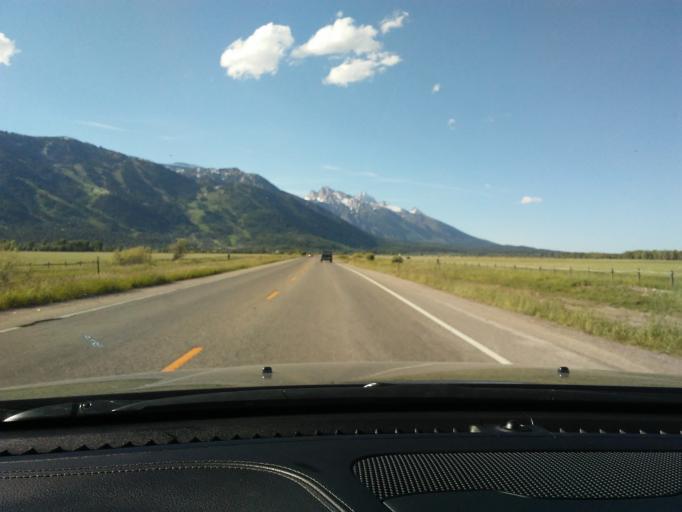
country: US
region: Wyoming
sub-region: Teton County
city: Moose Wilson Road
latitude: 43.5604
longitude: -110.8221
